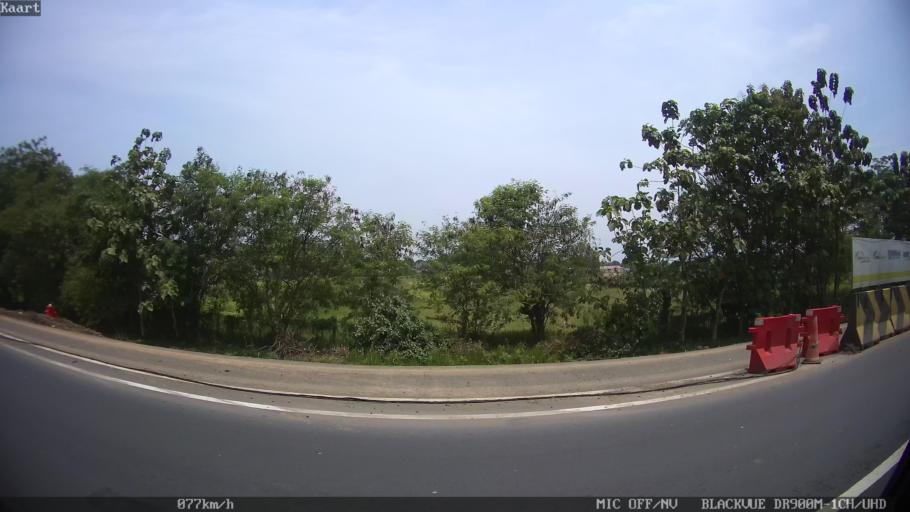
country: ID
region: West Java
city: Kresek
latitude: -6.1407
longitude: 106.2665
